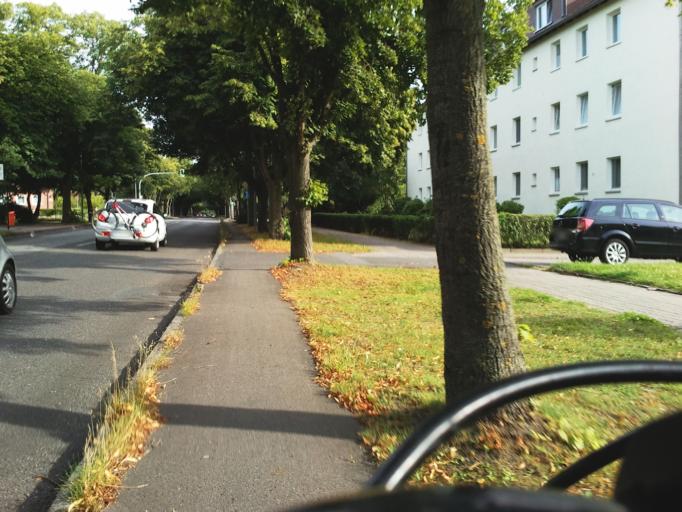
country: DE
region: Mecklenburg-Vorpommern
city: Kritzmow
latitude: 54.0947
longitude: 12.0843
